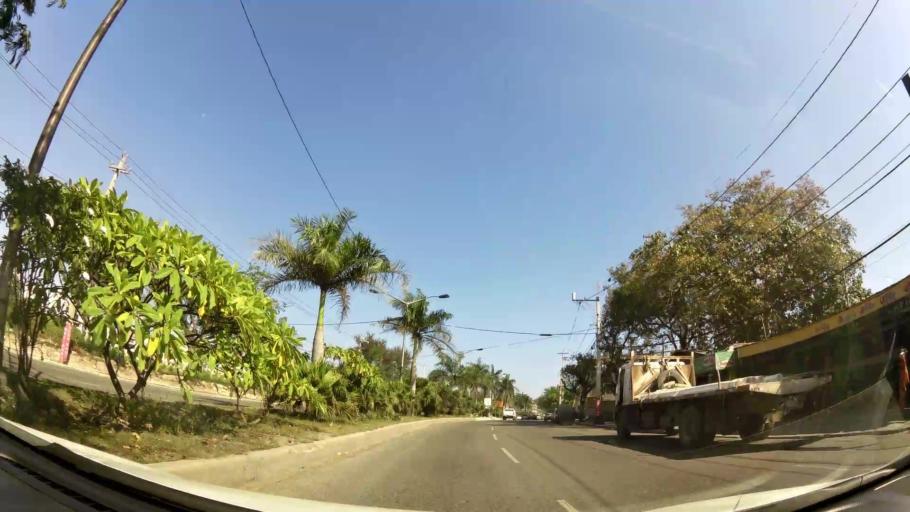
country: DO
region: Nacional
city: Bella Vista
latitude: 18.4590
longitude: -69.9854
